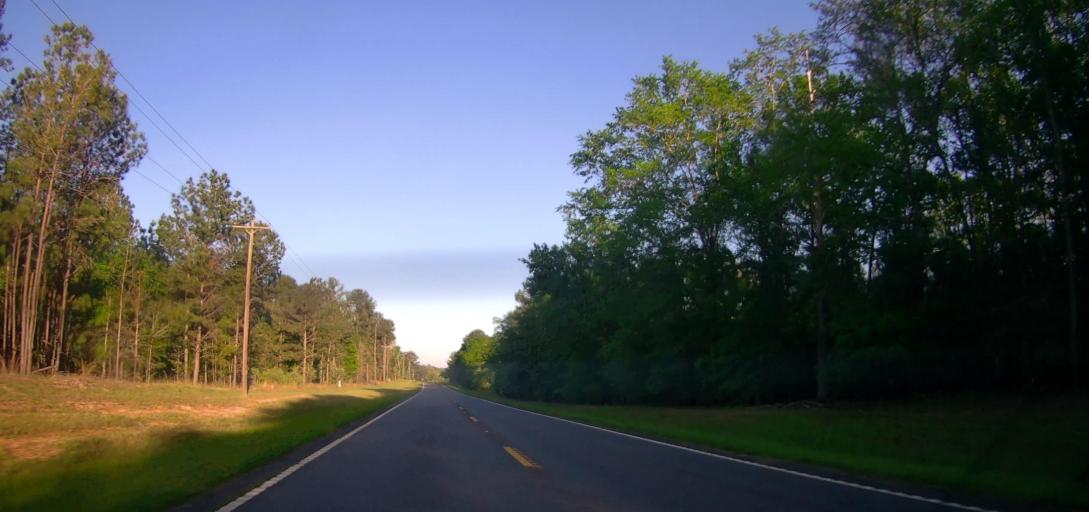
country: US
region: Georgia
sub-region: Schley County
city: Ellaville
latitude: 32.3306
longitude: -84.3391
